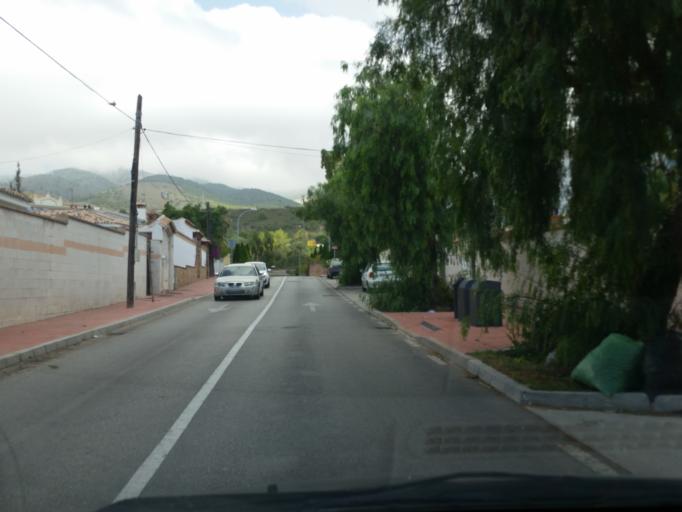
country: ES
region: Andalusia
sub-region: Provincia de Malaga
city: Torremolinos
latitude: 36.6042
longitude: -4.5259
